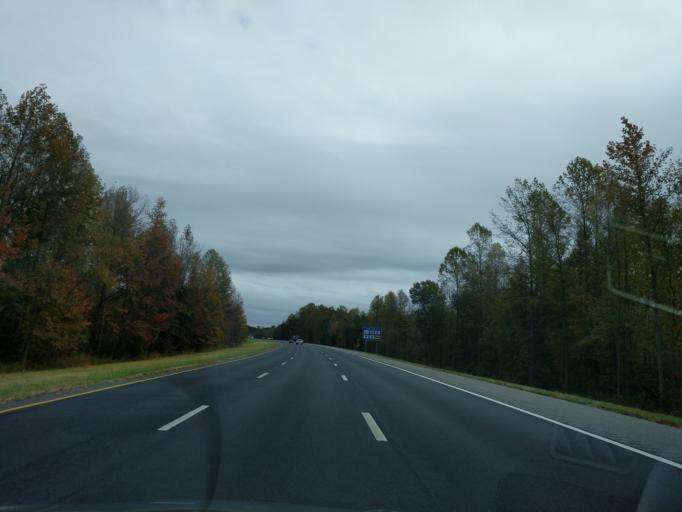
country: US
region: North Carolina
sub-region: Davidson County
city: Lexington
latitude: 35.7766
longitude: -80.2754
